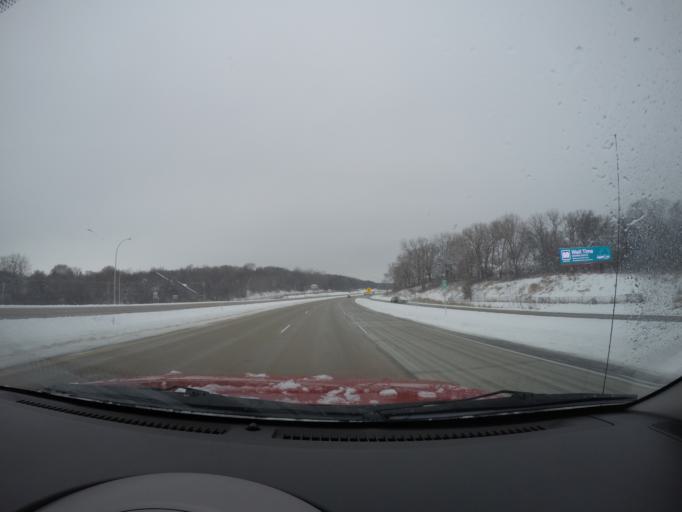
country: US
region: Minnesota
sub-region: Olmsted County
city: Rochester
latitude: 43.9773
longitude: -92.4652
